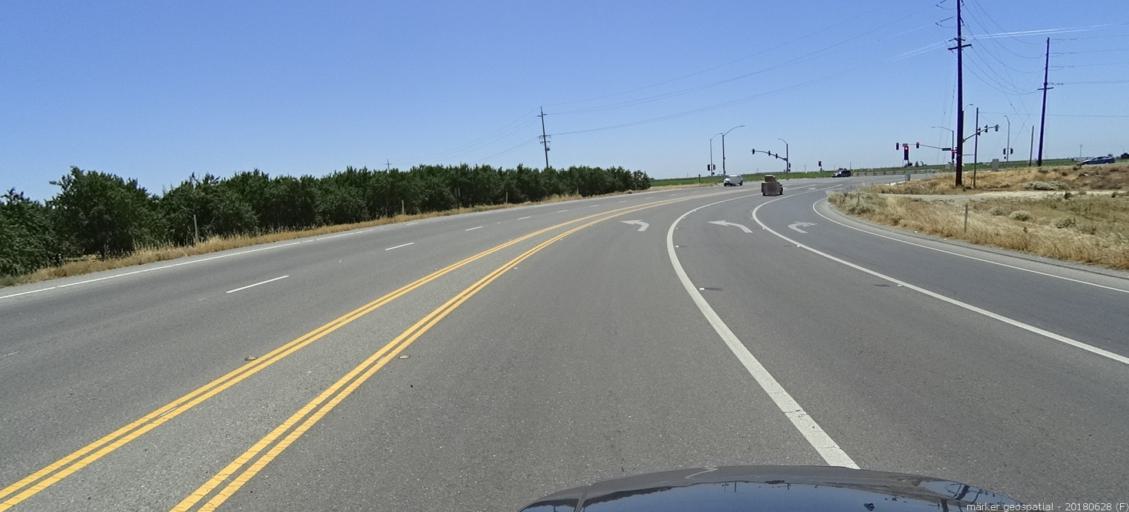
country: US
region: California
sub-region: Madera County
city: Parksdale
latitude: 36.9247
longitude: -120.0163
